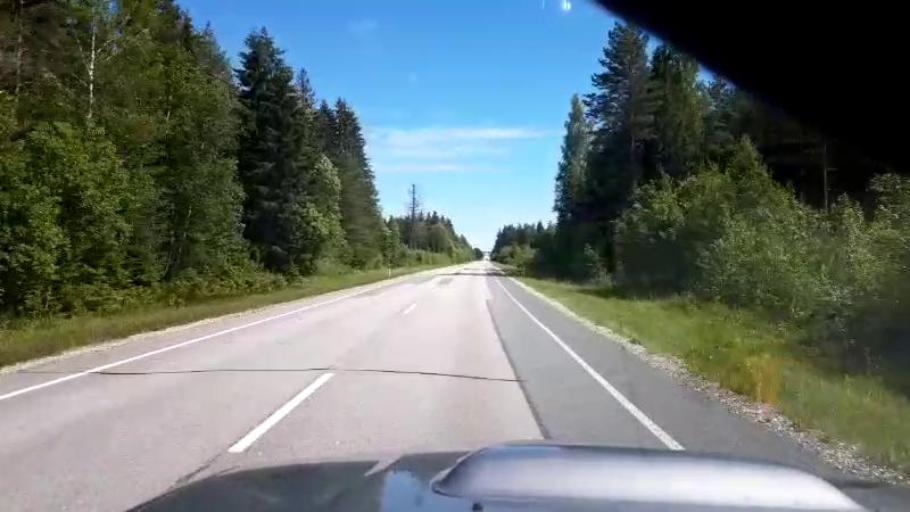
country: EE
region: Jaervamaa
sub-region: Koeru vald
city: Koeru
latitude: 58.9722
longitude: 26.1277
